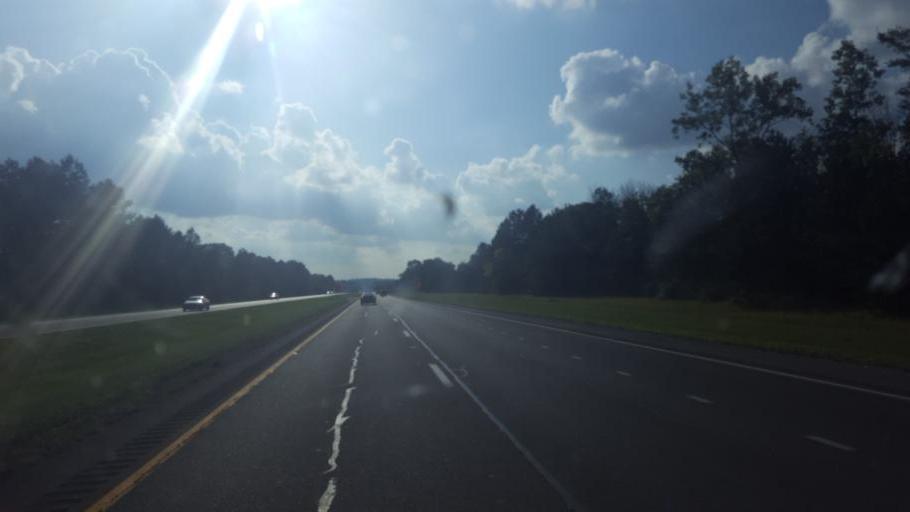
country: US
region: Ohio
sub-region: Richland County
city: Lincoln Heights
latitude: 40.7794
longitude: -82.4765
